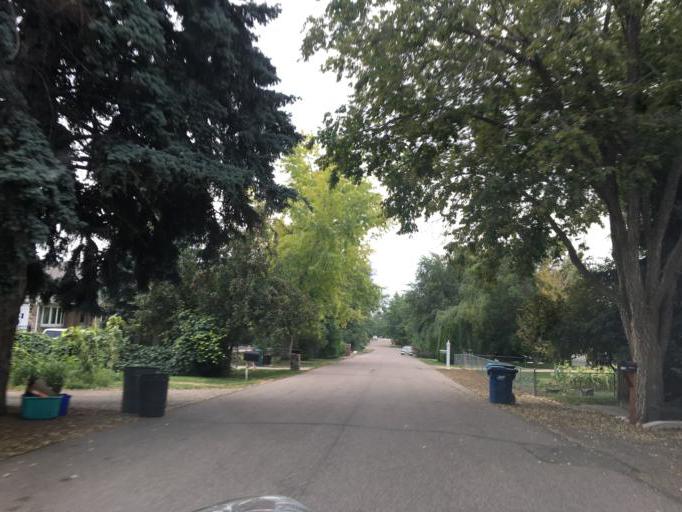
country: US
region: Colorado
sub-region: Jefferson County
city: Wheat Ridge
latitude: 39.7491
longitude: -105.0920
